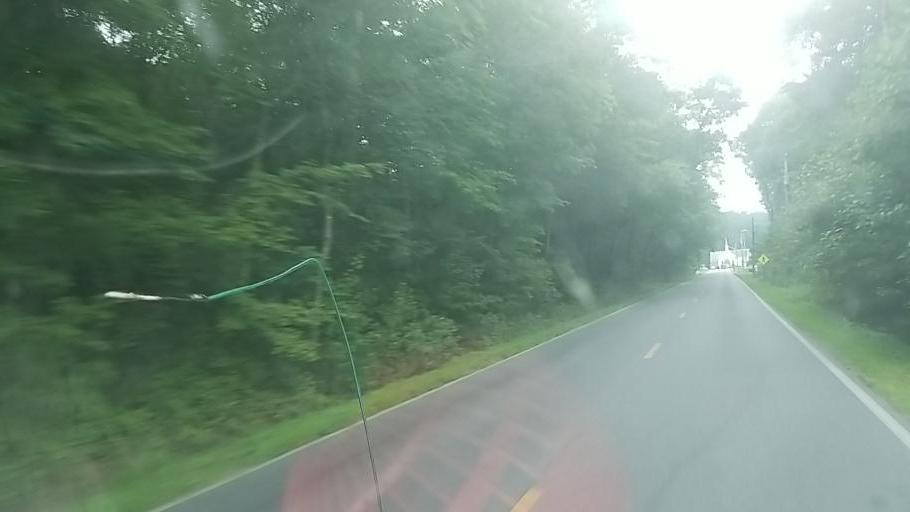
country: US
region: Maryland
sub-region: Wicomico County
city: Delmar
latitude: 38.3972
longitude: -75.5325
